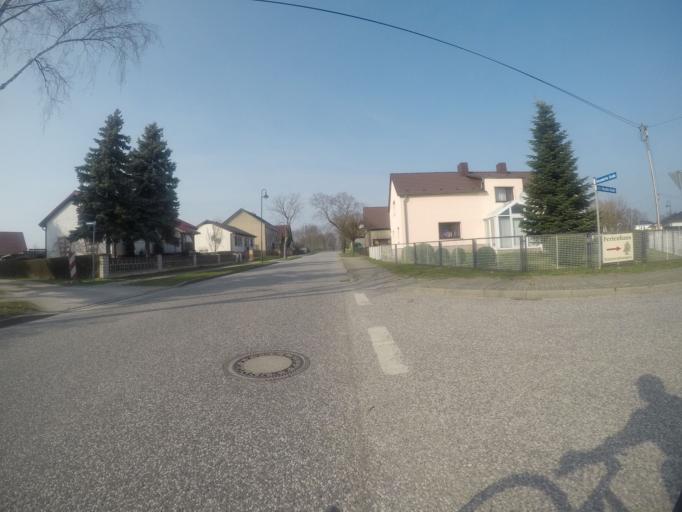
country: DE
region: Brandenburg
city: Mittenwalde
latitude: 52.3107
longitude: 13.5120
